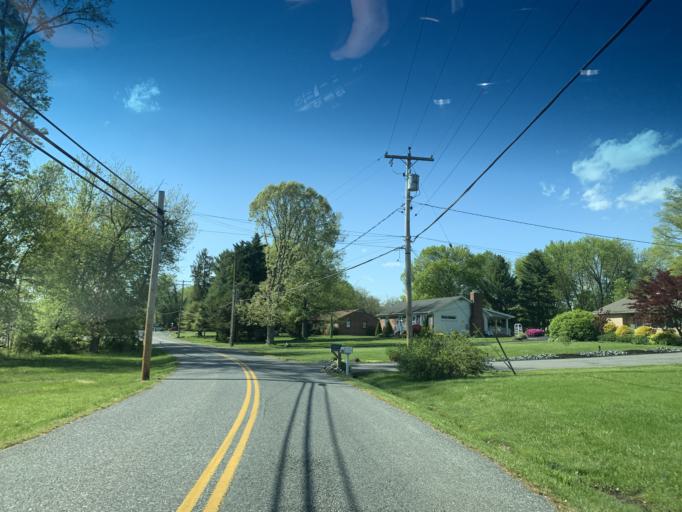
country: US
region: Maryland
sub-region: Harford County
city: Riverside
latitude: 39.4554
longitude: -76.2492
